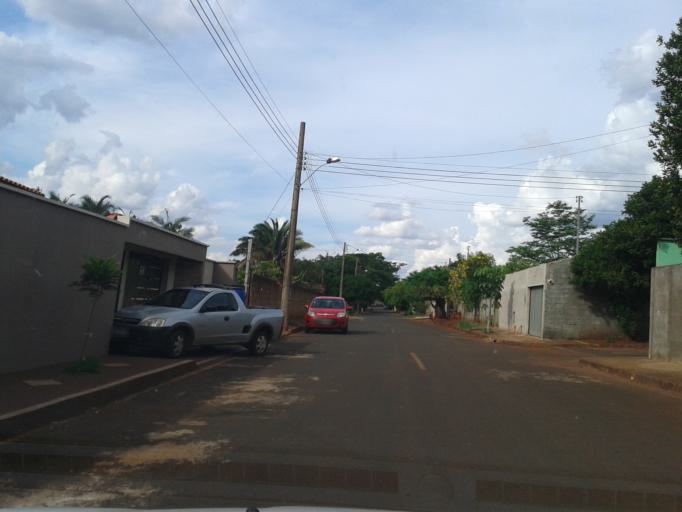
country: BR
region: Minas Gerais
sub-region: Centralina
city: Centralina
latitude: -18.7251
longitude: -49.2080
